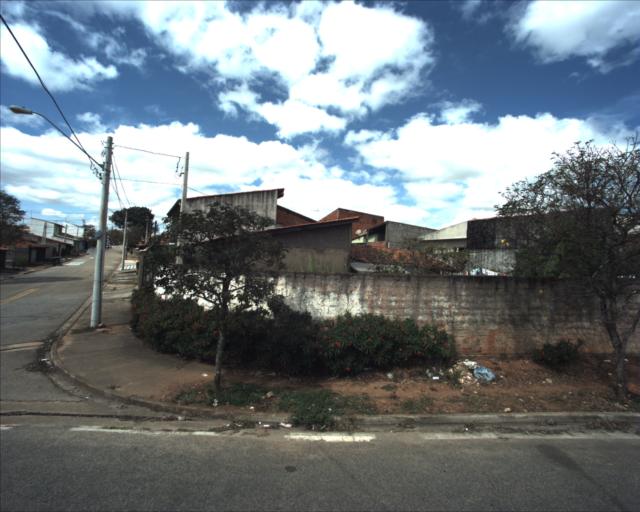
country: BR
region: Sao Paulo
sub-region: Sorocaba
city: Sorocaba
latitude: -23.5041
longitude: -47.5223
